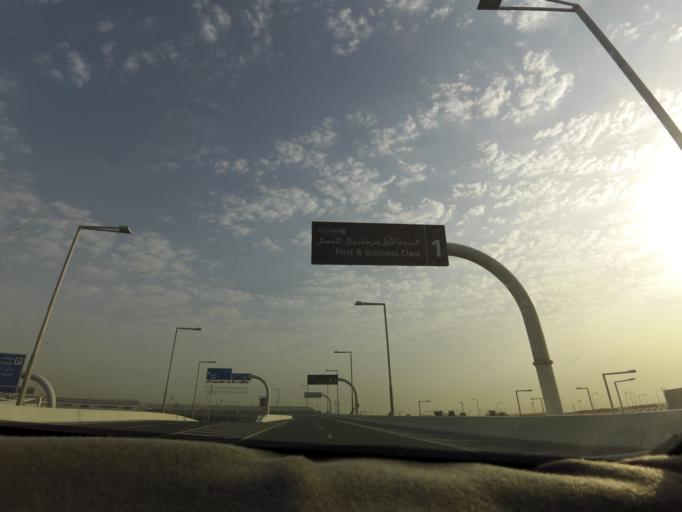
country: QA
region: Al Wakrah
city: Al Wakrah
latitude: 25.2583
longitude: 51.6171
